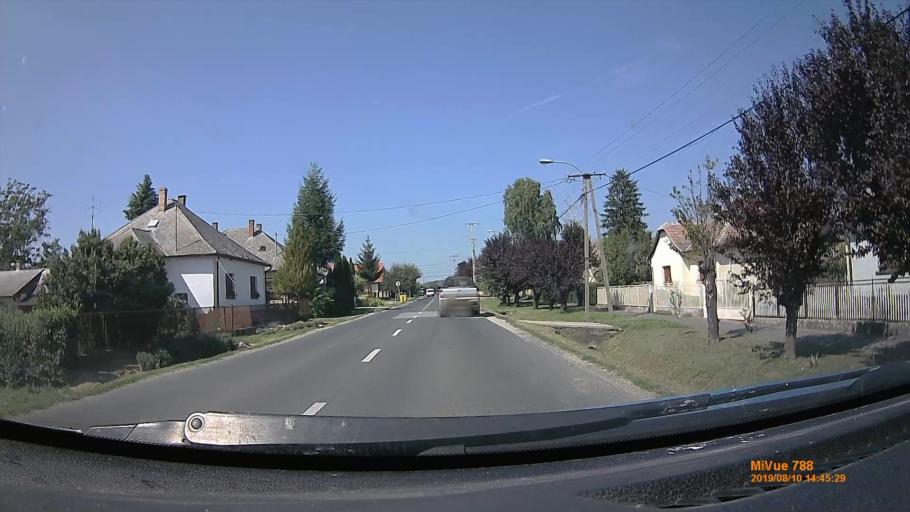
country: HU
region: Somogy
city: Somogyvar
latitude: 46.5852
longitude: 17.6451
